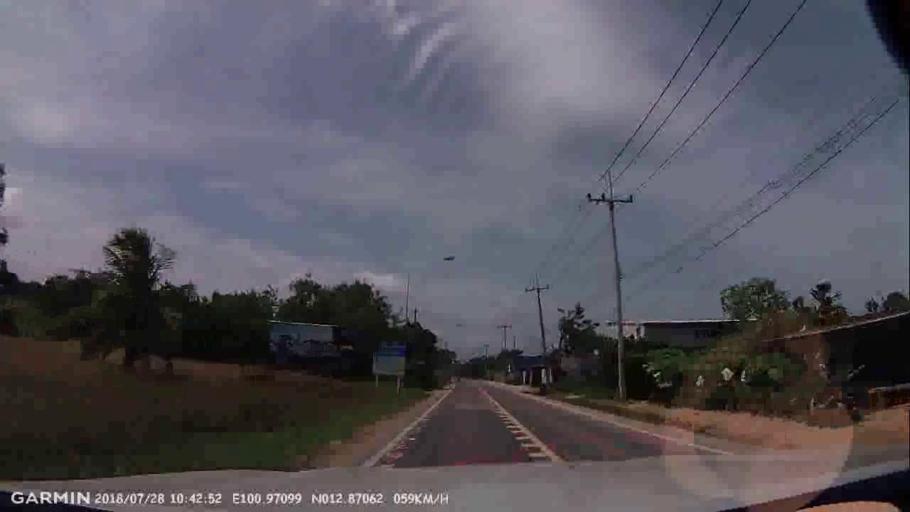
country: TH
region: Chon Buri
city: Phatthaya
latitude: 12.8704
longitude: 100.9710
